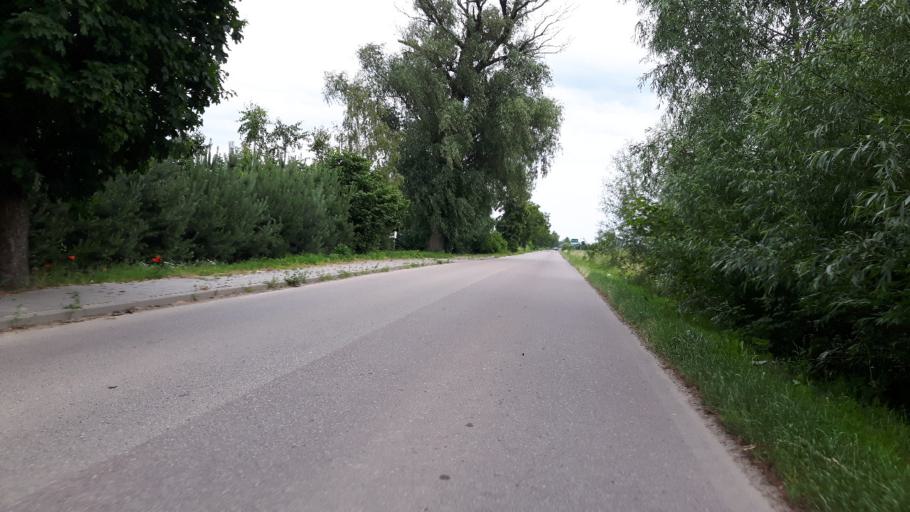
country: PL
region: Warmian-Masurian Voivodeship
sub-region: Powiat elblaski
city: Gronowo Elblaskie
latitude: 54.2119
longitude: 19.2654
